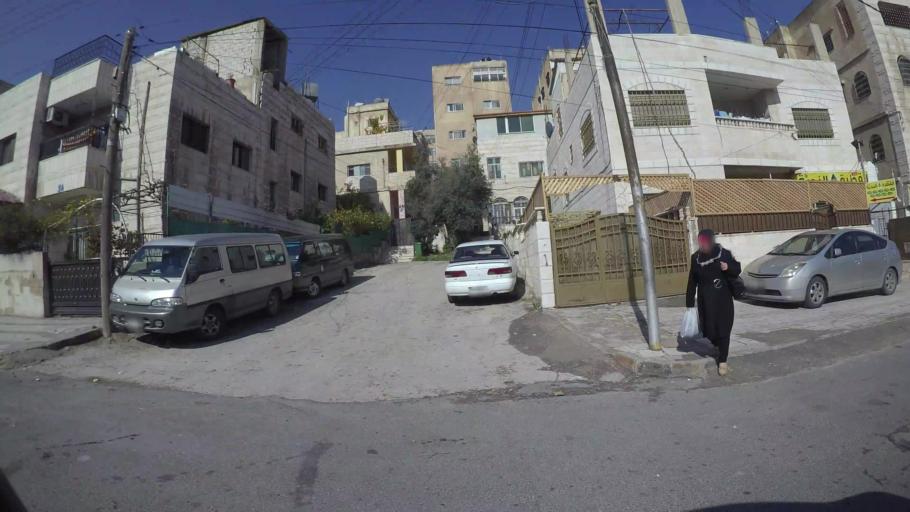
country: JO
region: Amman
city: Amman
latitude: 31.9348
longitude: 35.9090
